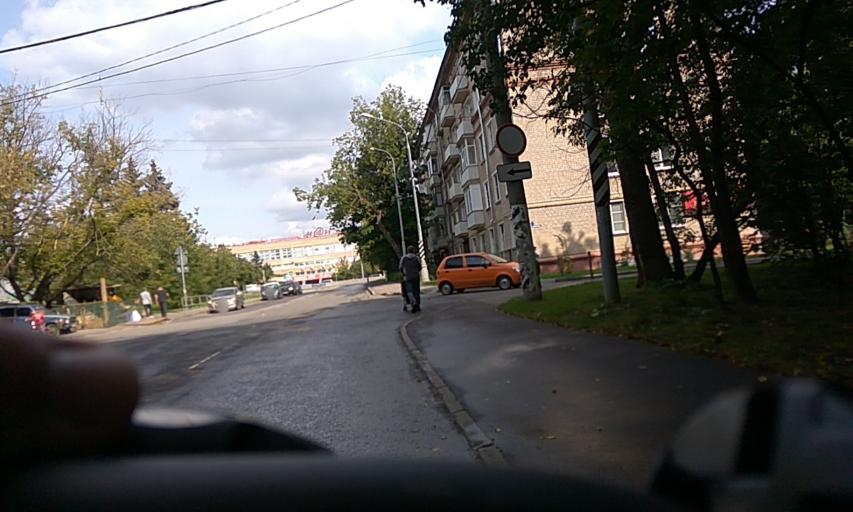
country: RU
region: Moscow
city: Tsaritsyno
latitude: 55.6479
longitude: 37.6623
